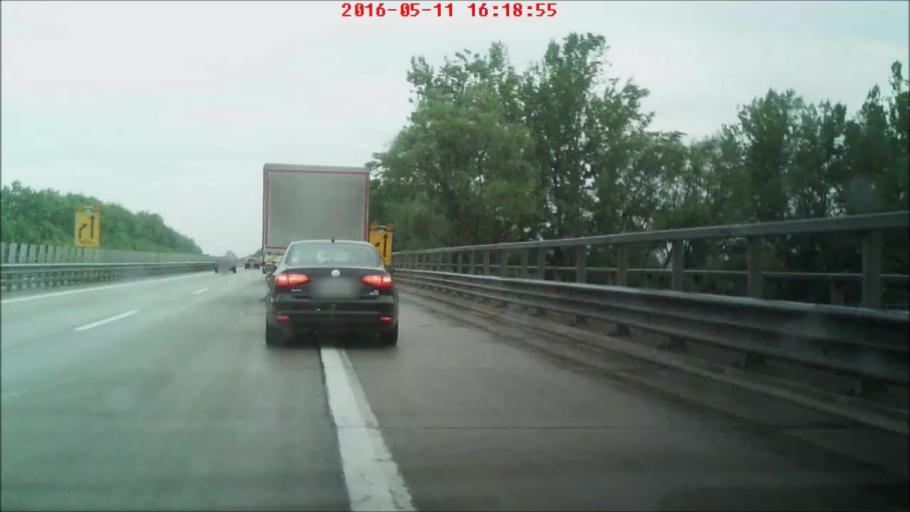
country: AT
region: Styria
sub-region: Politischer Bezirk Leibnitz
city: Gabersdorf
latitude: 46.7774
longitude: 15.5791
